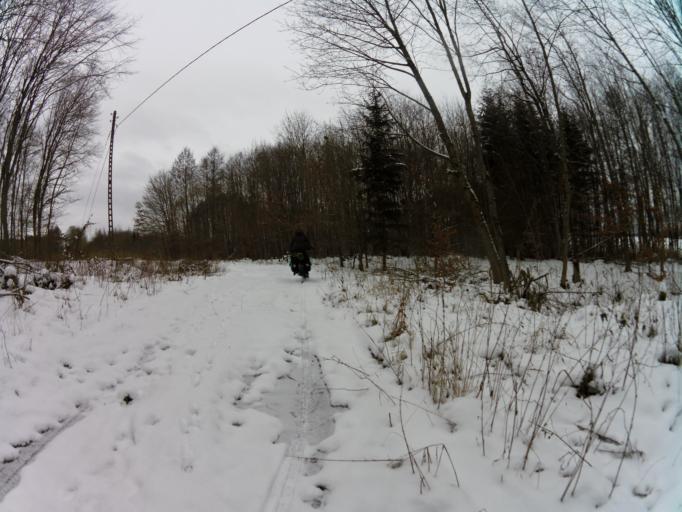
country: PL
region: West Pomeranian Voivodeship
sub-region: Powiat choszczenski
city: Recz
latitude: 53.3323
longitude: 15.5454
